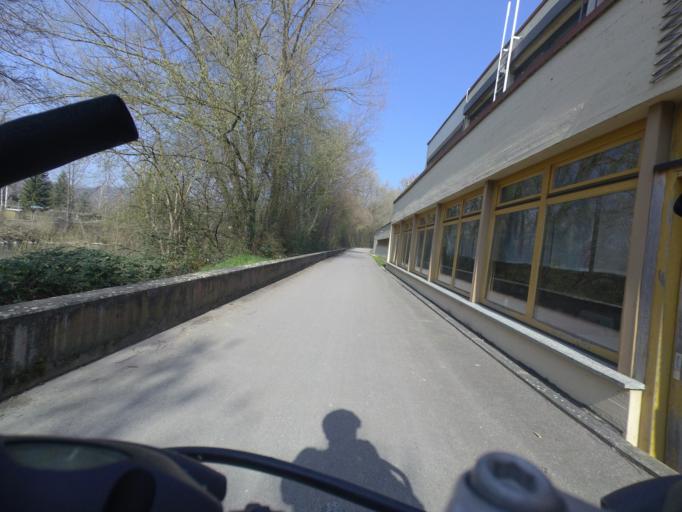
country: DE
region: Baden-Wuerttemberg
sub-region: Regierungsbezirk Stuttgart
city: Nurtingen
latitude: 48.6333
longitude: 9.3318
